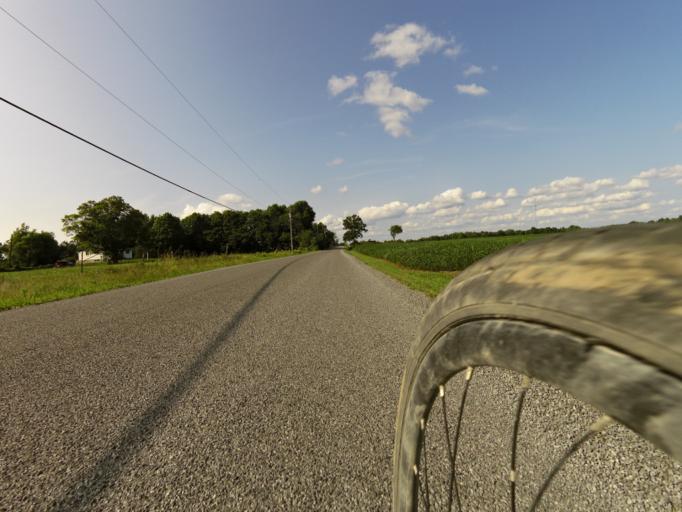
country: CA
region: Ontario
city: Kingston
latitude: 44.3900
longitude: -76.5960
